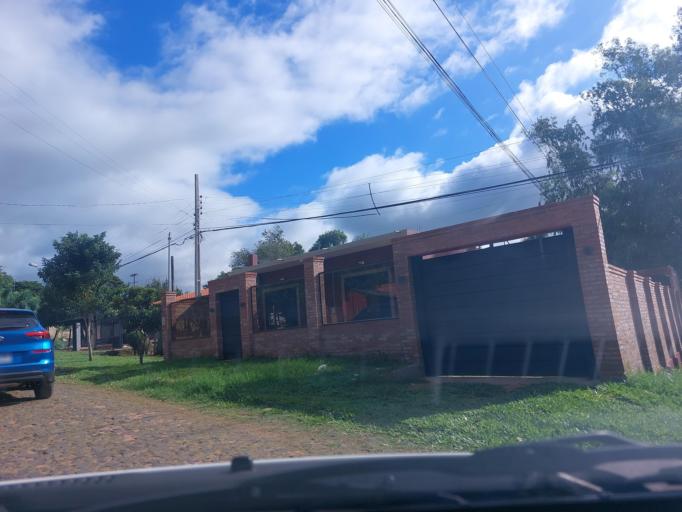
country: PY
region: San Pedro
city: Guayaybi
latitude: -24.6701
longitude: -56.4397
